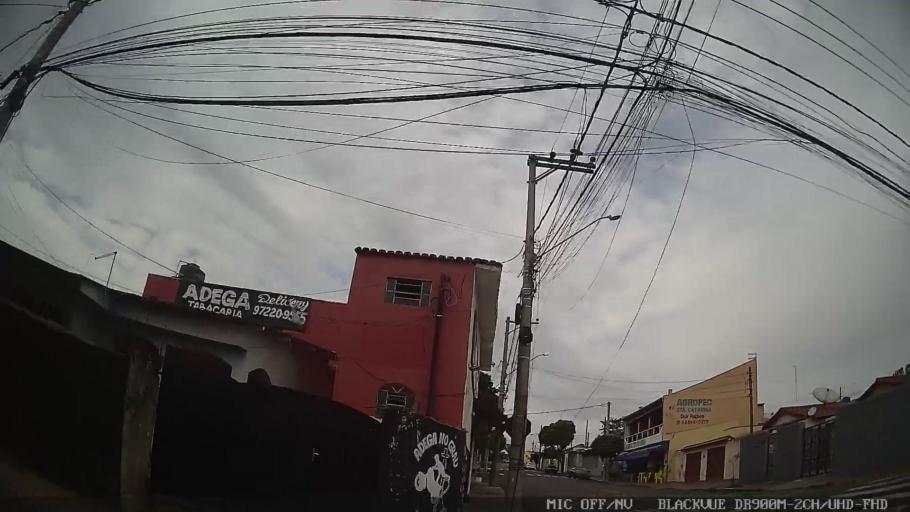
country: BR
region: Sao Paulo
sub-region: Salto
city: Salto
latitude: -23.2193
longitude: -47.2651
